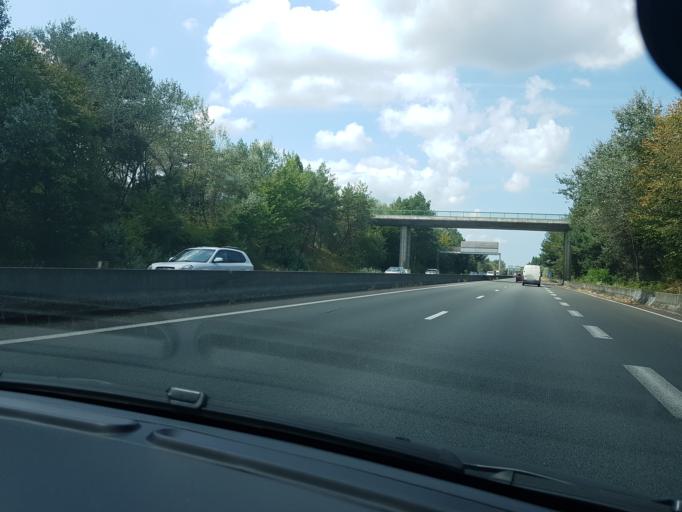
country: FR
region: Aquitaine
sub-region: Departement de la Gironde
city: Arveyres
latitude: 44.8754
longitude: -0.2892
